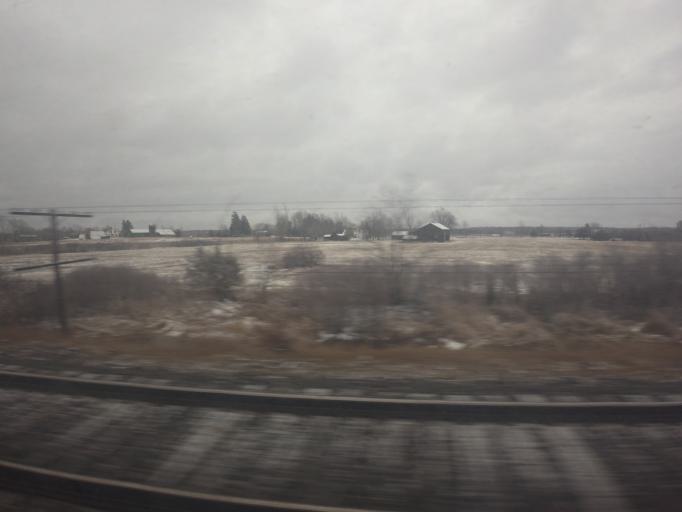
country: CA
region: Ontario
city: Gananoque
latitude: 44.3868
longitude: -76.0560
